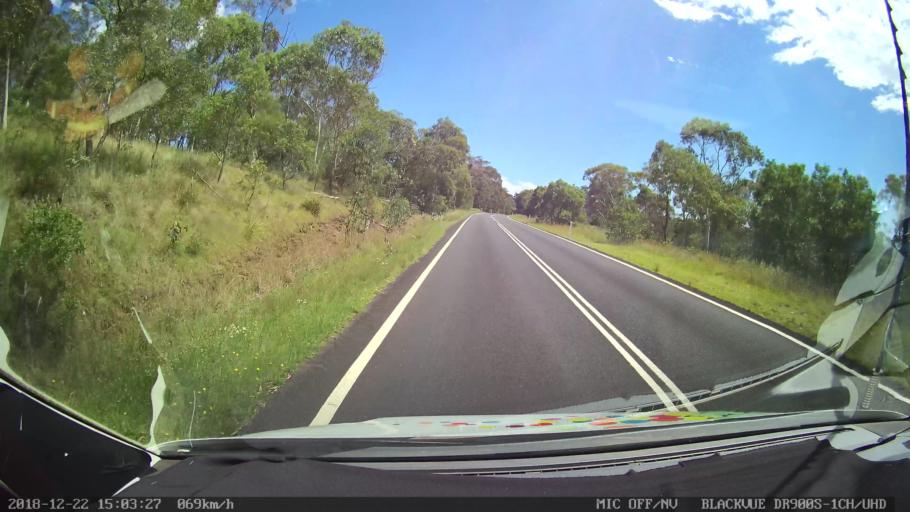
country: AU
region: New South Wales
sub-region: Bellingen
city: Dorrigo
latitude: -30.2646
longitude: 152.4408
